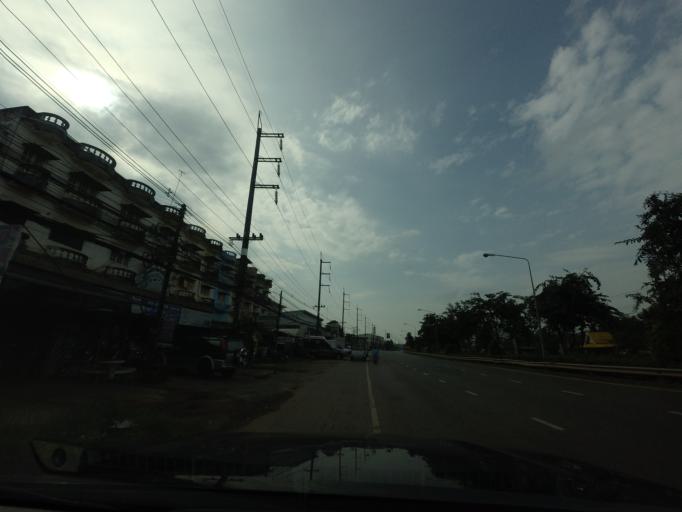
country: TH
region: Nong Khai
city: Nong Khai
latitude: 17.8633
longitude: 102.7488
